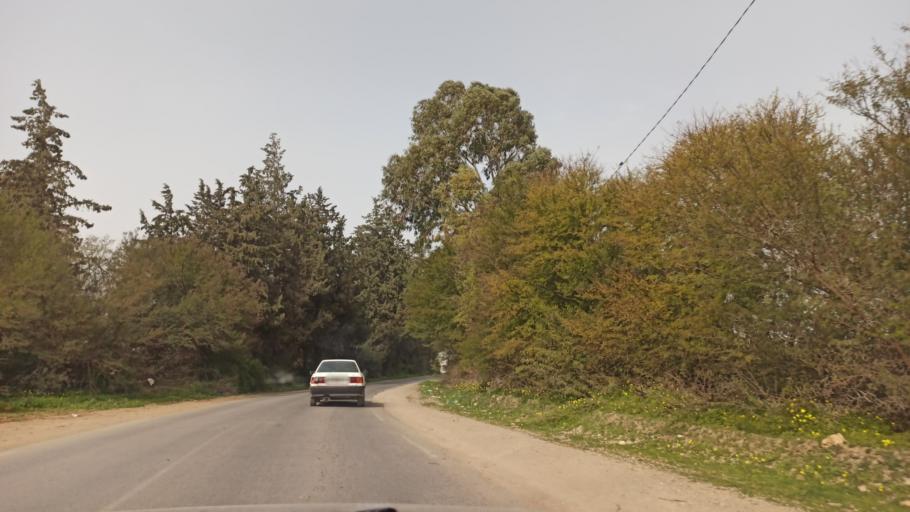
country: TN
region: Zaghwan
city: Zaghouan
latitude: 36.4223
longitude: 10.0959
